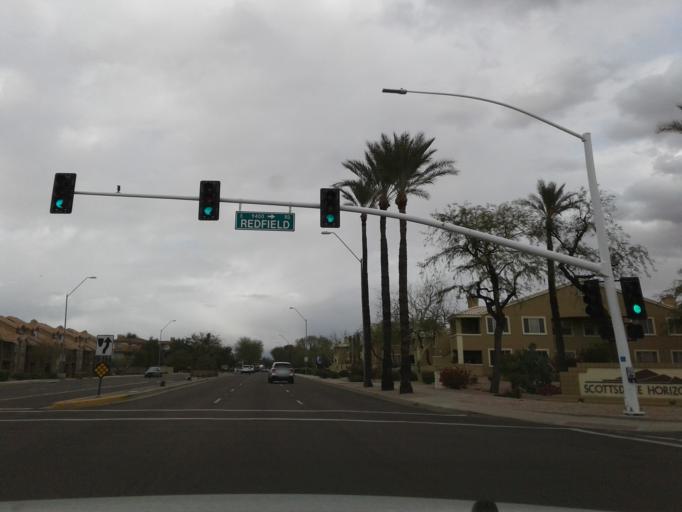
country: US
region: Arizona
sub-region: Maricopa County
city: Paradise Valley
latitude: 33.6149
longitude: -111.8783
